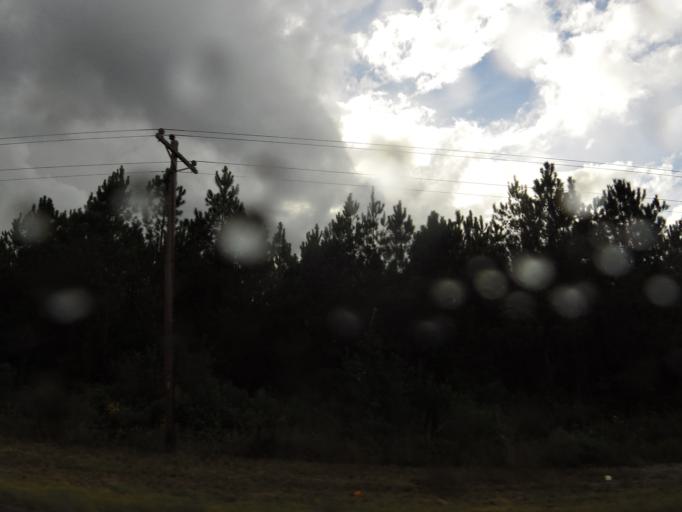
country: US
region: Florida
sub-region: Nassau County
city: Hilliard
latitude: 30.5680
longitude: -82.0441
